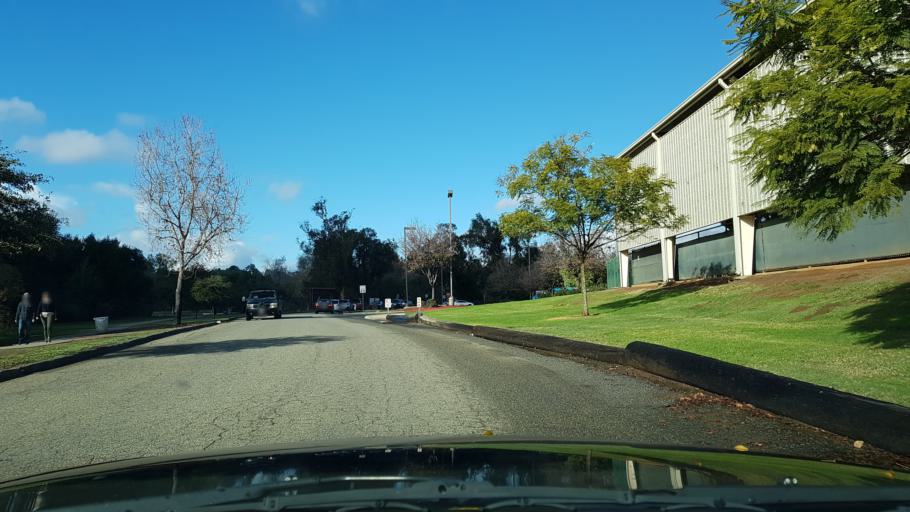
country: US
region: California
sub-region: San Diego County
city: Escondido
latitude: 33.0769
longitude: -117.0605
